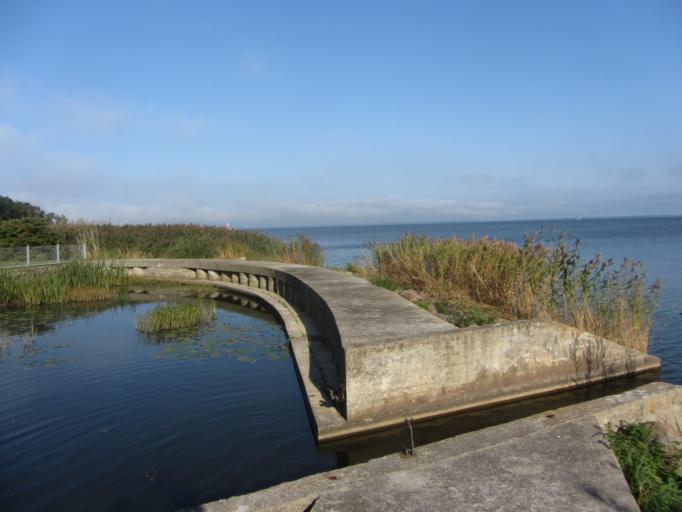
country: LT
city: Neringa
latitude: 55.4161
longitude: 21.1016
